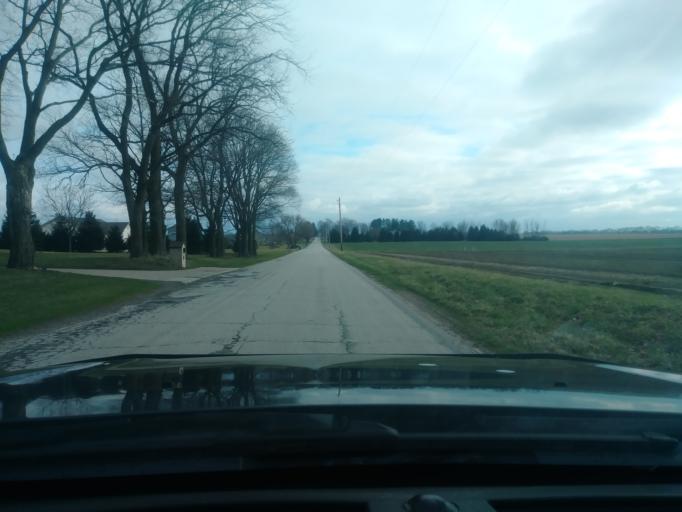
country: US
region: Indiana
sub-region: LaPorte County
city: LaPorte
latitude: 41.5879
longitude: -86.7980
